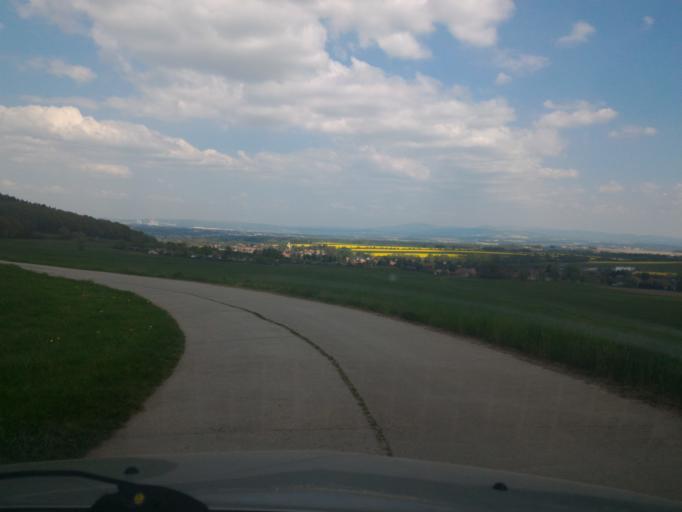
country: DE
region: Saxony
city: Kurort Jonsdorf
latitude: 50.8806
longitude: 14.7076
